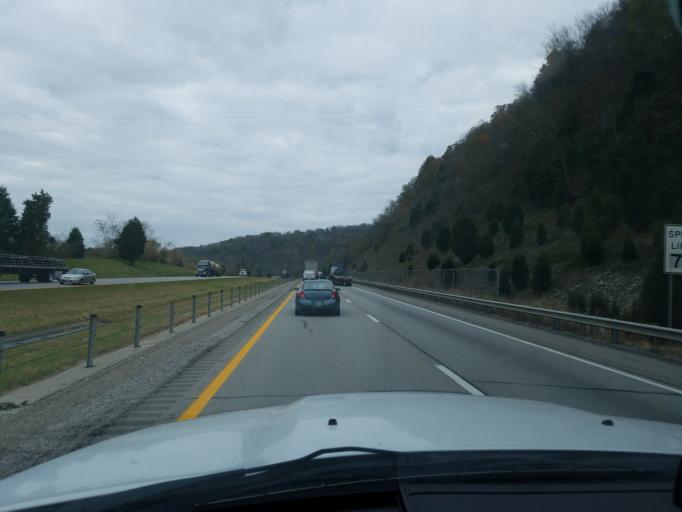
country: US
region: Kentucky
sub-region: Carroll County
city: Carrollton
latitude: 38.6282
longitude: -85.1472
